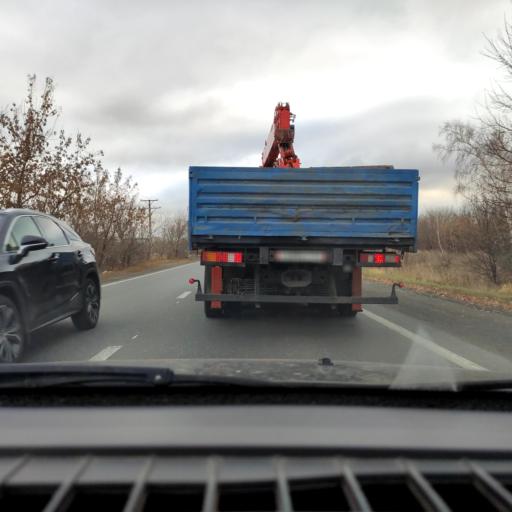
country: RU
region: Samara
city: Tol'yatti
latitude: 53.5577
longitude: 49.3623
